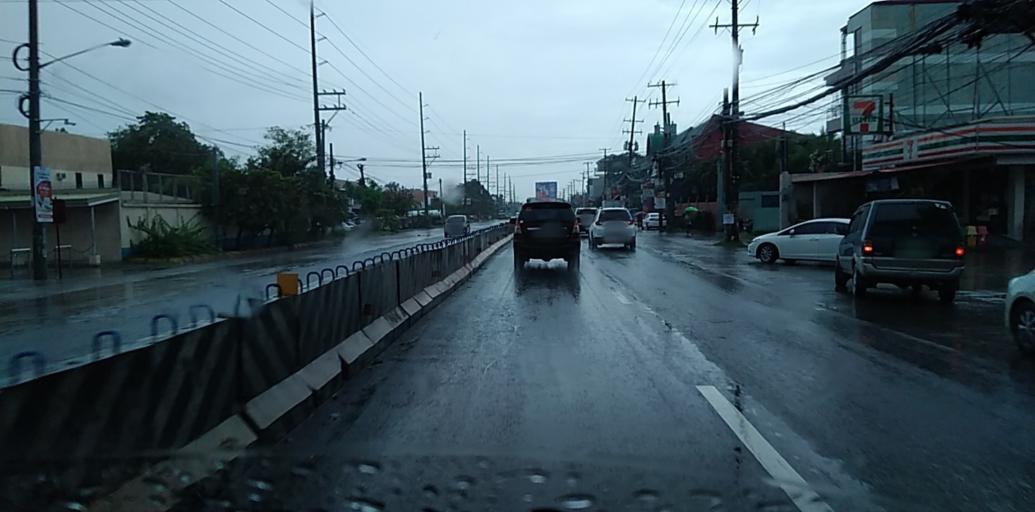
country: PH
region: Central Luzon
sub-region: Province of Pampanga
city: Magliman
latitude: 15.0527
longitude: 120.6626
